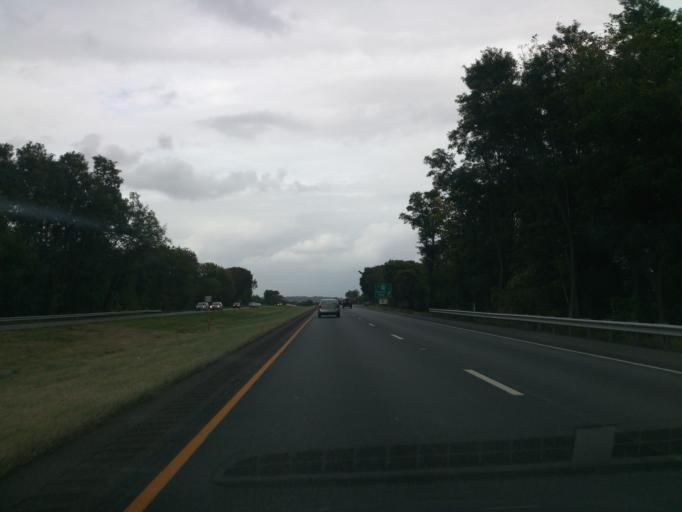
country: US
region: Pennsylvania
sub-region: Lancaster County
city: Brownstown
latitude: 40.0967
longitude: -76.2597
